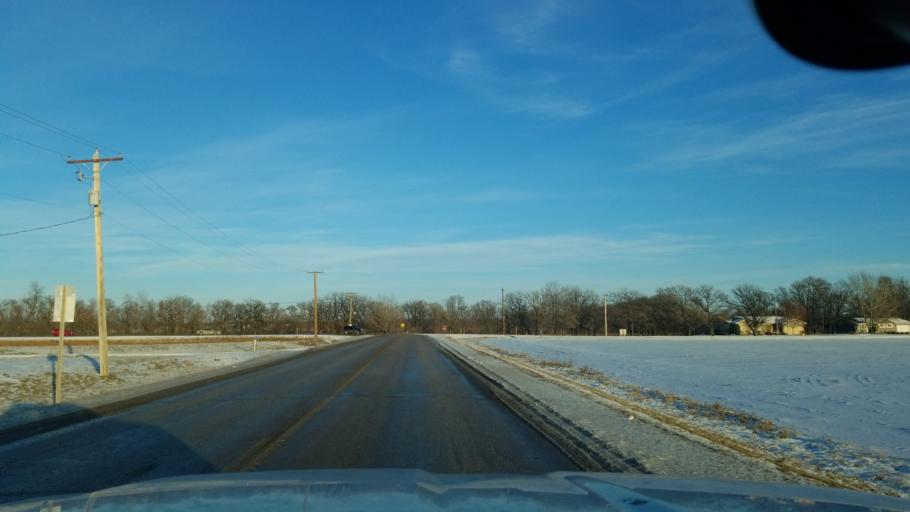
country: CA
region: Manitoba
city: Portage la Prairie
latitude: 49.9570
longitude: -98.3222
